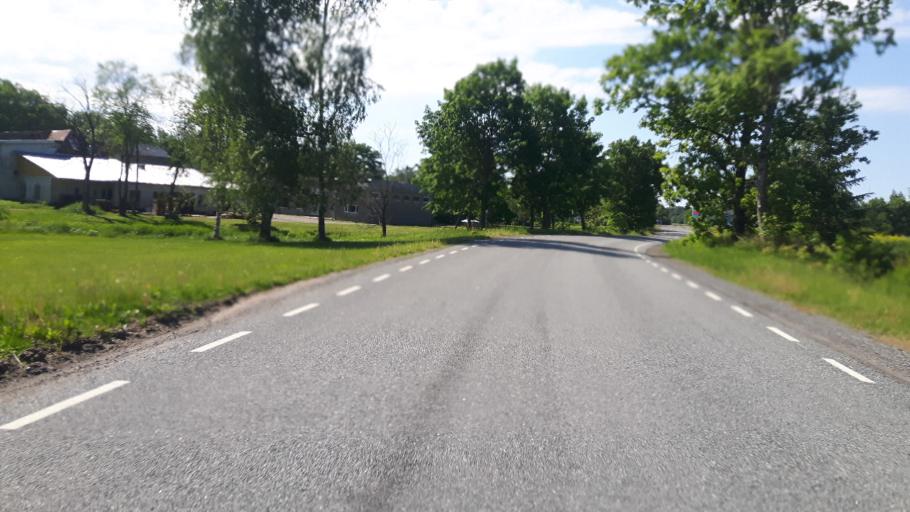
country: EE
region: Paernumaa
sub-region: Vaendra vald (alev)
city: Vandra
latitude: 58.6546
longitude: 25.0247
